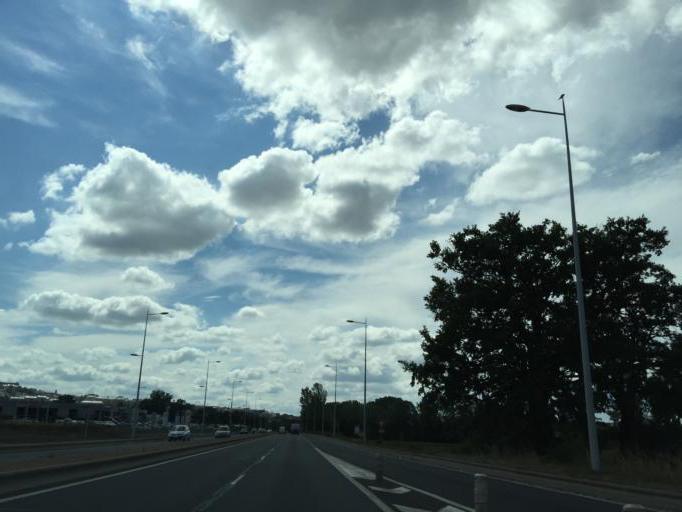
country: FR
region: Midi-Pyrenees
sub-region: Departement de l'Aveyron
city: Rodez
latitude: 44.3716
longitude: 2.5850
